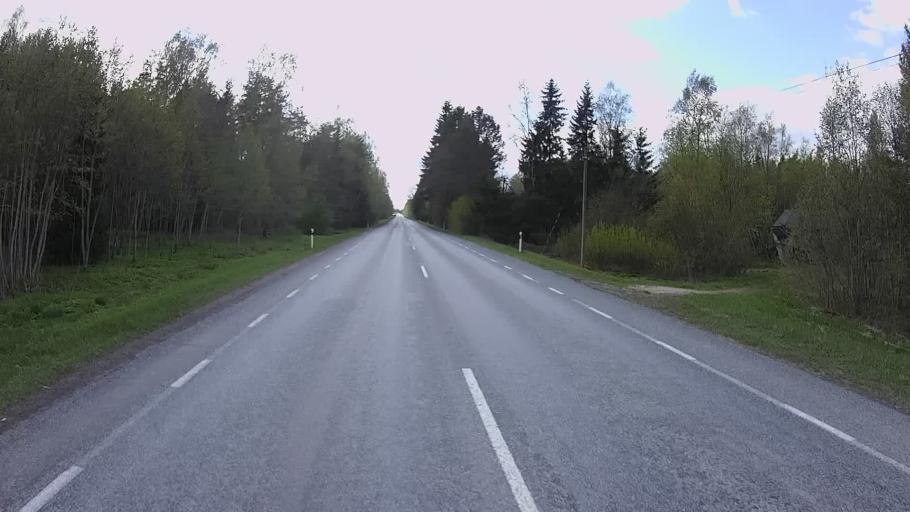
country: EE
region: Tartu
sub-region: Tartu linn
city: Tartu
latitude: 58.5117
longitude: 26.9334
